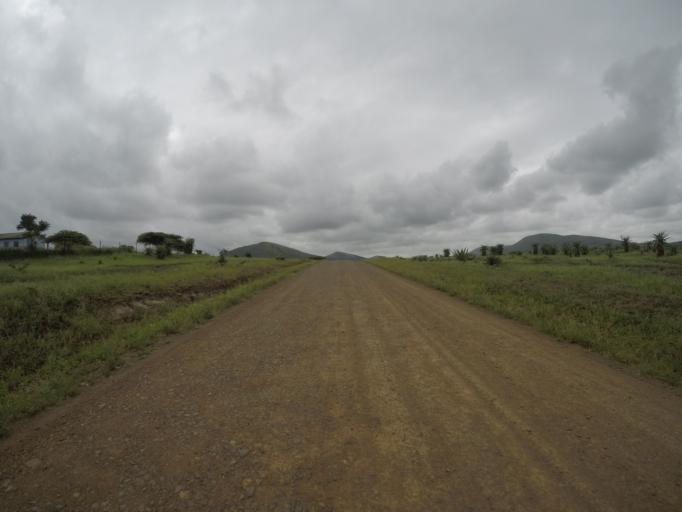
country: ZA
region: KwaZulu-Natal
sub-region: uThungulu District Municipality
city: Empangeni
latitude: -28.6092
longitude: 31.8675
